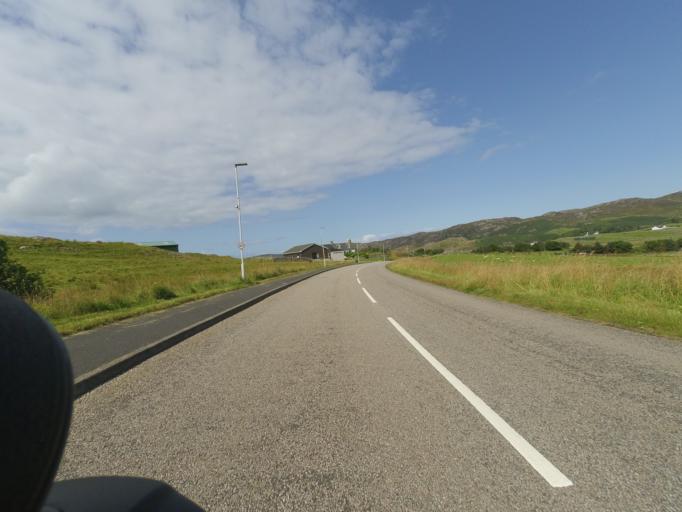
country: GB
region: Scotland
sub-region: Highland
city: Ullapool
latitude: 58.3463
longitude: -5.1607
